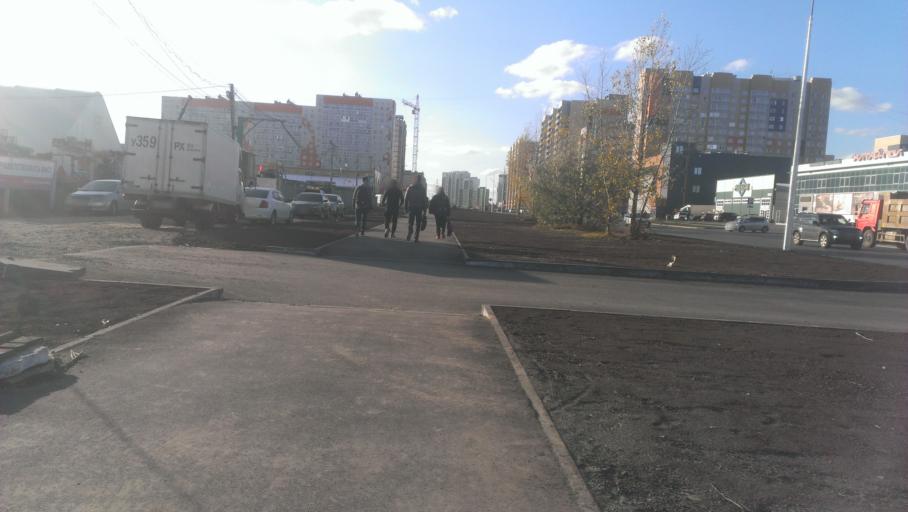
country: RU
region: Altai Krai
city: Novosilikatnyy
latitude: 53.3364
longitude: 83.6639
